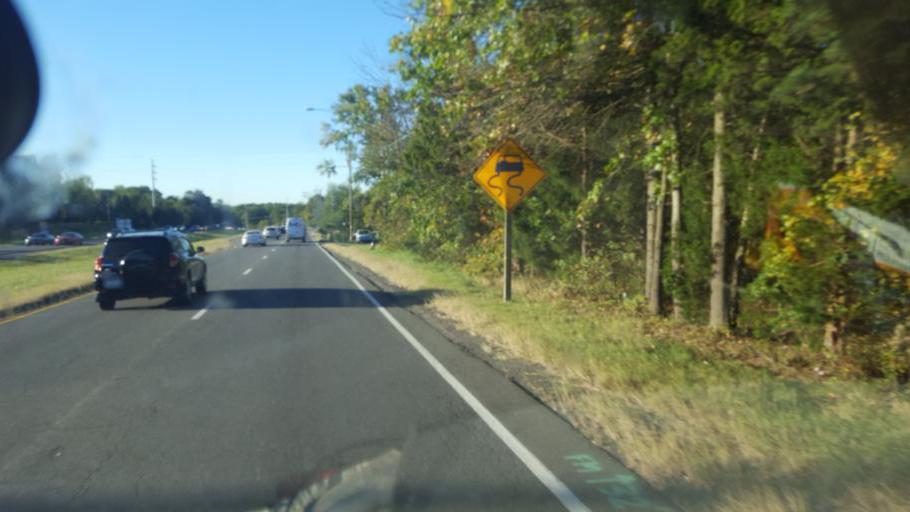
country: US
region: Virginia
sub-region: Prince William County
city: Yorkshire
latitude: 38.8090
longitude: -77.4492
